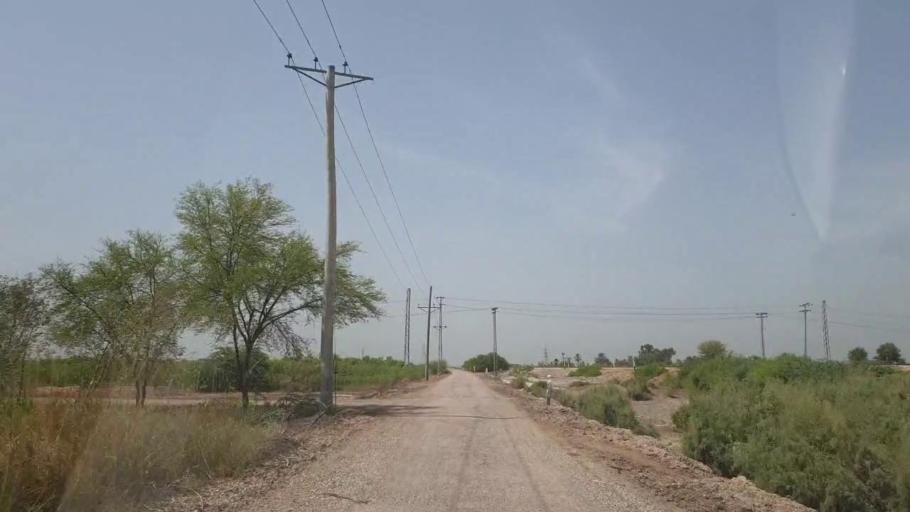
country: PK
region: Sindh
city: Gambat
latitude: 27.3203
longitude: 68.5363
